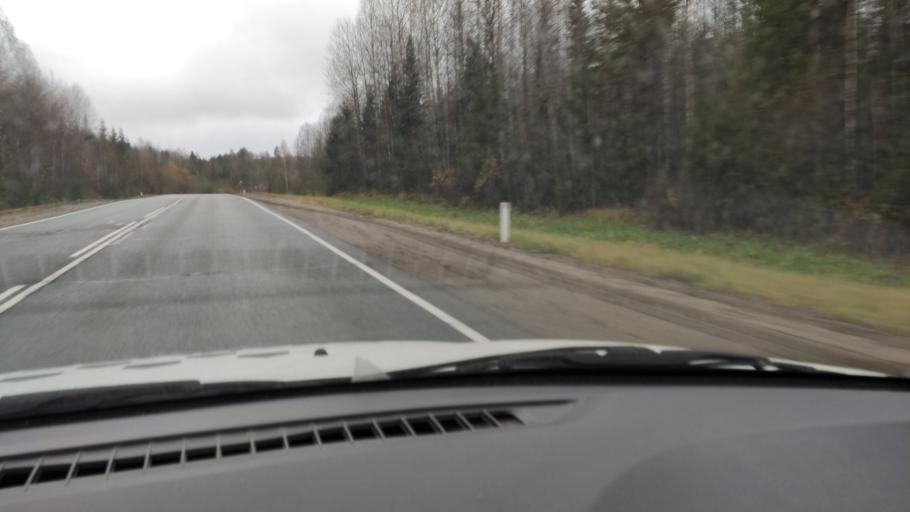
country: RU
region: Kirov
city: Chernaya Kholunitsa
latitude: 58.8915
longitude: 51.3455
